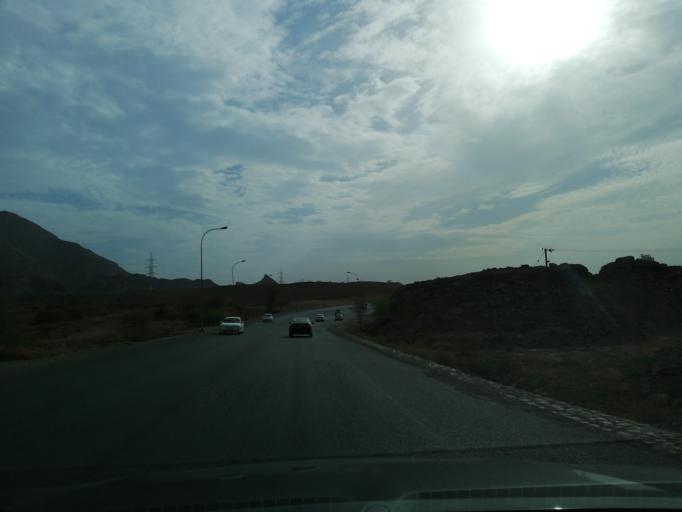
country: OM
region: Muhafazat Masqat
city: Bawshar
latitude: 23.4777
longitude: 58.2982
